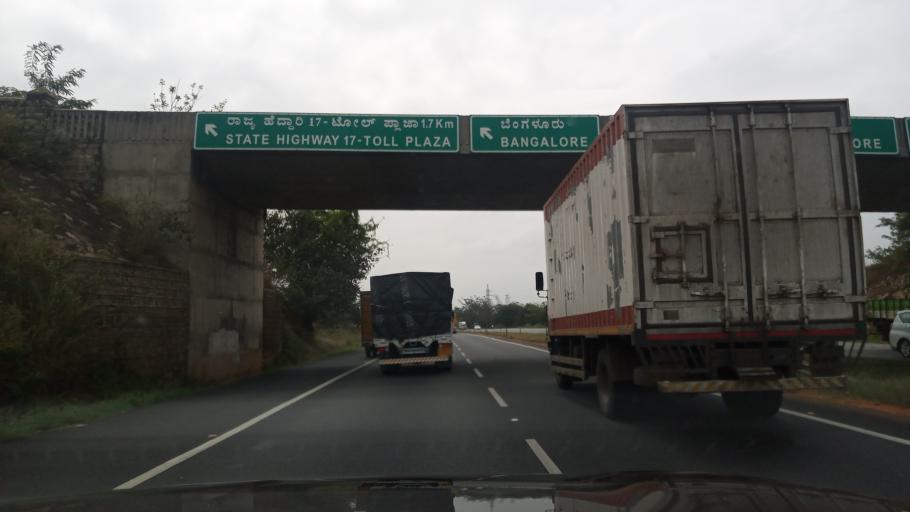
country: IN
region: Karnataka
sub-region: Bangalore Urban
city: Bangalore
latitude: 12.9151
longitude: 77.4678
